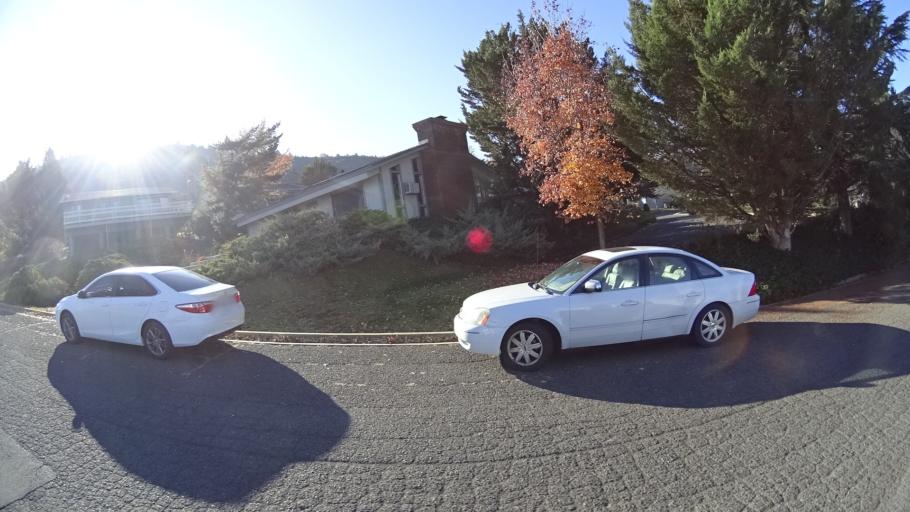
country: US
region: California
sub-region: Siskiyou County
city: Yreka
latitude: 41.7325
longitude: -122.6236
